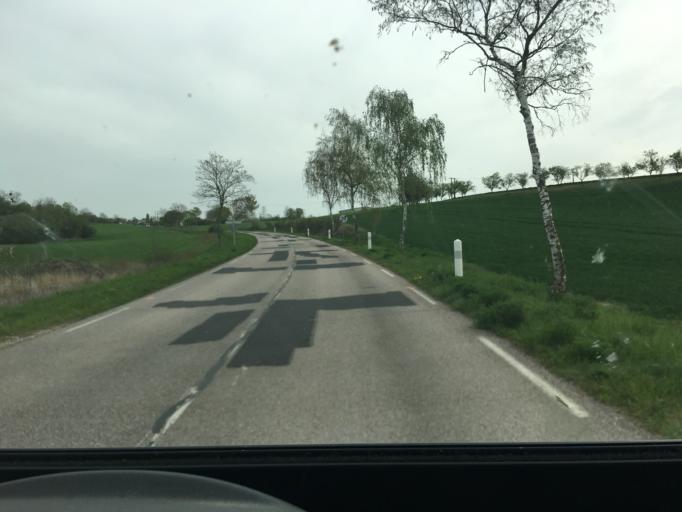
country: FR
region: Lorraine
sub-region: Departement de Meurthe-et-Moselle
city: Einville-au-Jard
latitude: 48.6550
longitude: 6.4733
